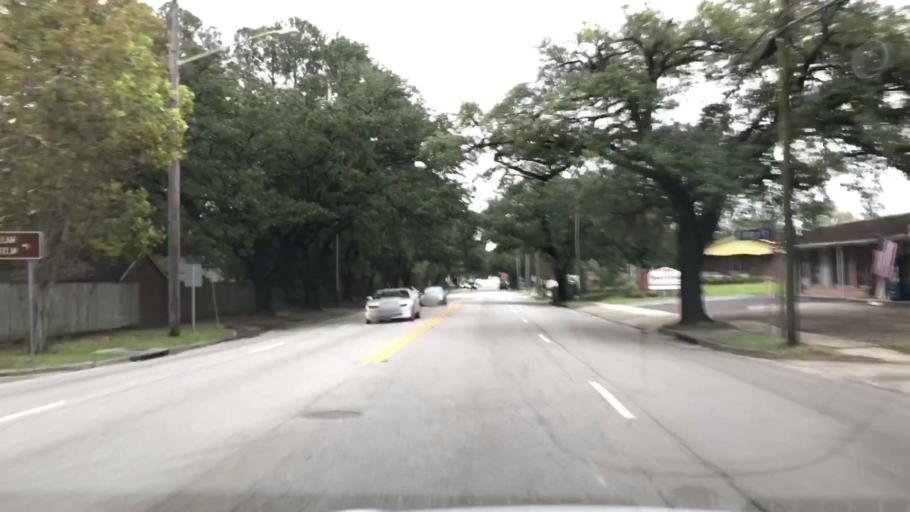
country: US
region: South Carolina
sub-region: Georgetown County
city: Georgetown
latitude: 33.3726
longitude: -79.2816
